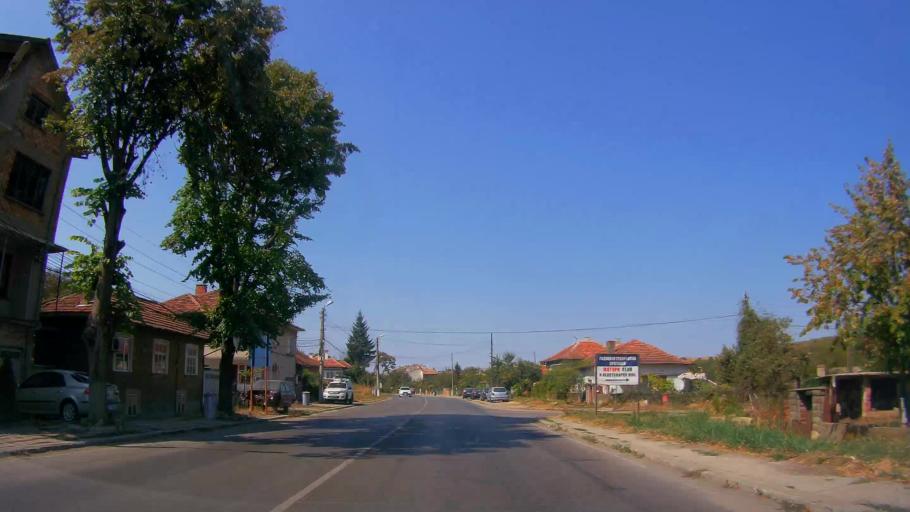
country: BG
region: Razgrad
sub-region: Obshtina Tsar Kaloyan
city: Tsar Kaloyan
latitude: 43.6105
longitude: 26.2337
